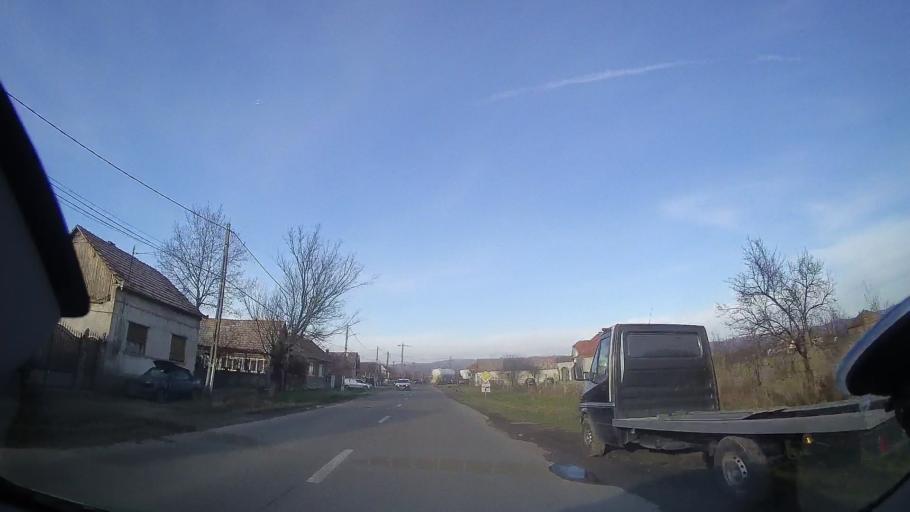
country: RO
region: Bihor
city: Lugasu de Jos
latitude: 47.0418
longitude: 22.3533
